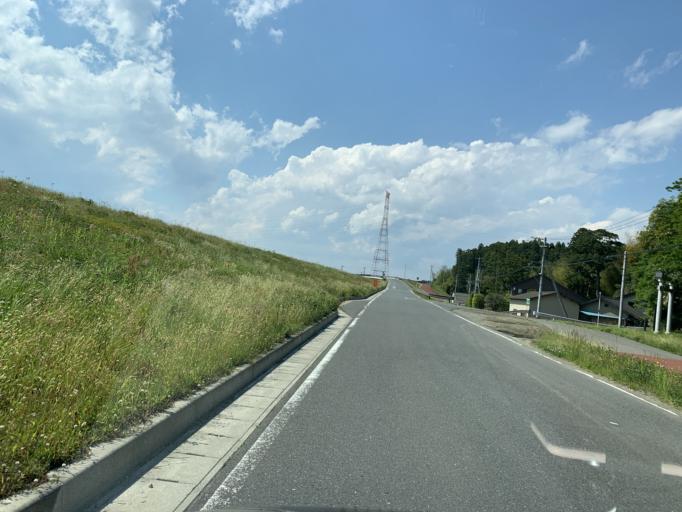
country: JP
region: Miyagi
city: Matsushima
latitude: 38.4268
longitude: 141.1267
